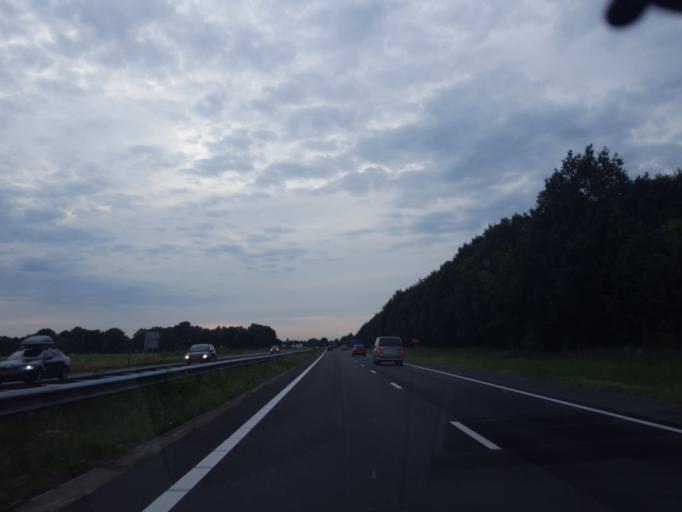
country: NL
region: Overijssel
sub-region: Gemeente Steenwijkerland
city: Steenwijk
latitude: 52.7771
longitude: 6.1708
